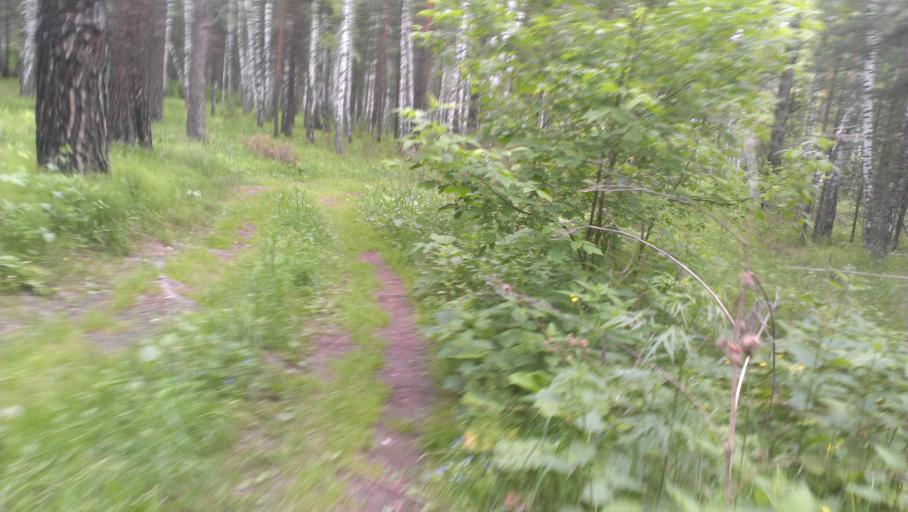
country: RU
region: Altai Krai
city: Sannikovo
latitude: 53.3422
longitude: 84.0460
